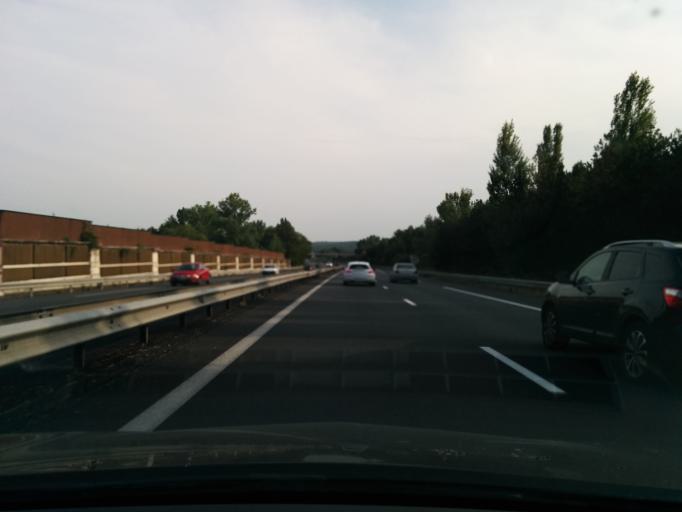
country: FR
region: Midi-Pyrenees
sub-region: Departement de la Haute-Garonne
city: Garidech
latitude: 43.7053
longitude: 1.5688
